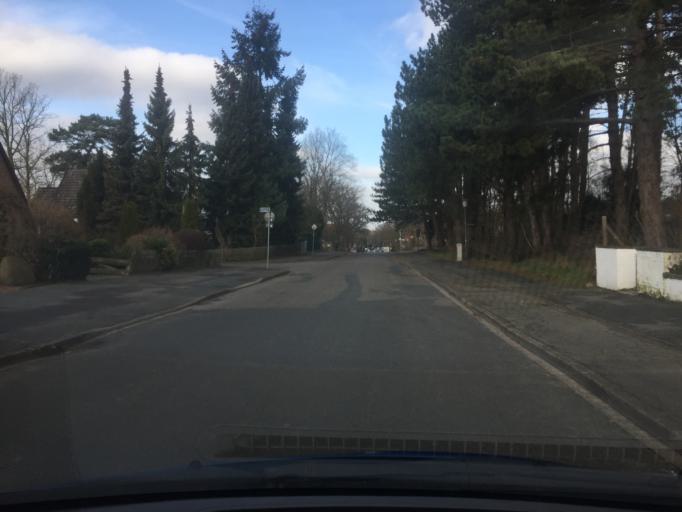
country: DE
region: Lower Saxony
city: Lueneburg
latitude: 53.2348
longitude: 10.4301
